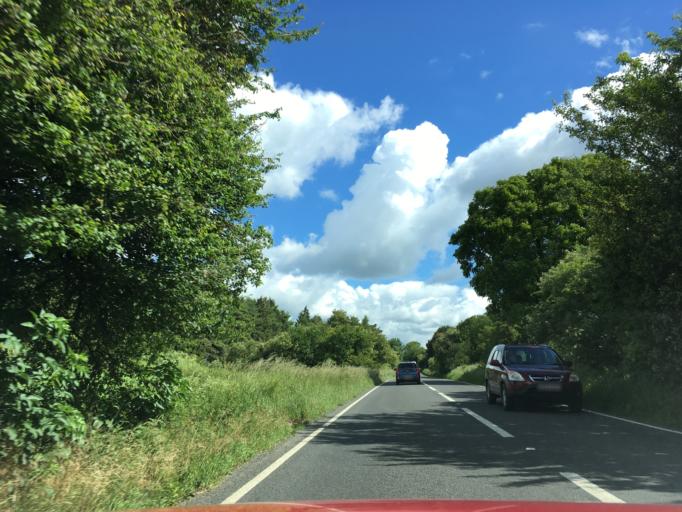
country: GB
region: England
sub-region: Oxfordshire
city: Burford
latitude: 51.7972
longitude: -1.6419
